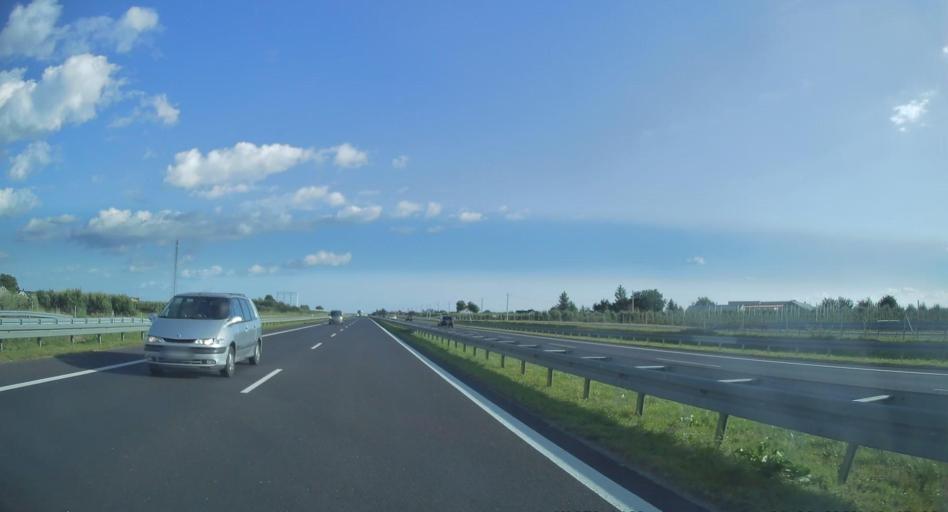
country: PL
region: Masovian Voivodeship
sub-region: Powiat grojecki
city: Jasieniec
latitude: 51.7806
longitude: 20.8961
